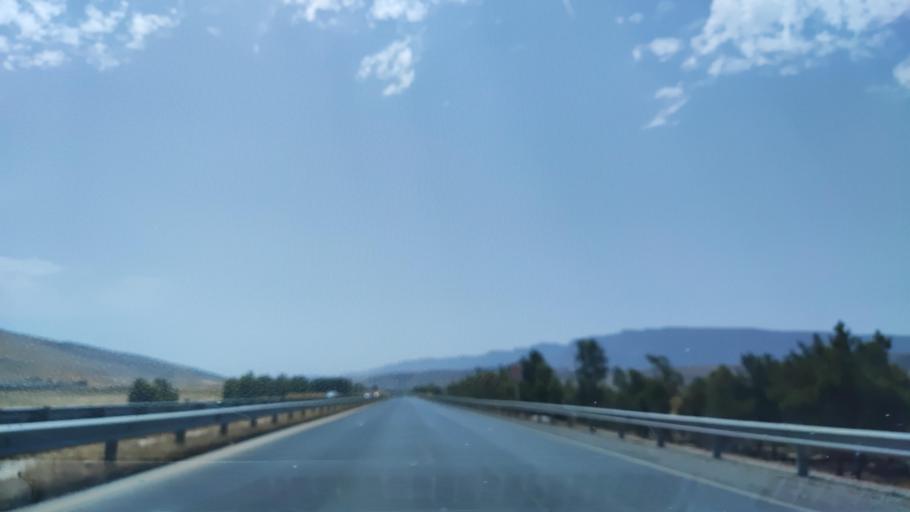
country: IQ
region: Arbil
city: Shaqlawah
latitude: 36.4748
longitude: 44.3809
